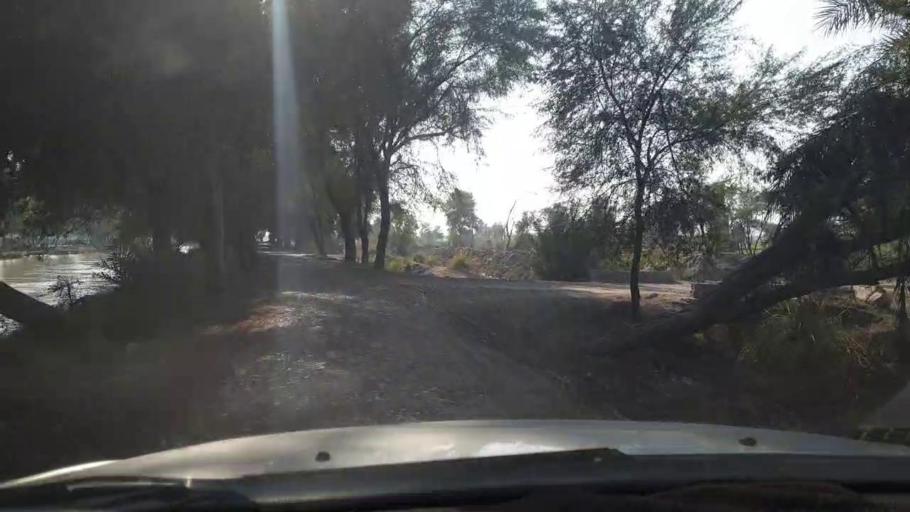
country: PK
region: Sindh
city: Mirpur Mathelo
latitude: 27.9927
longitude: 69.5467
